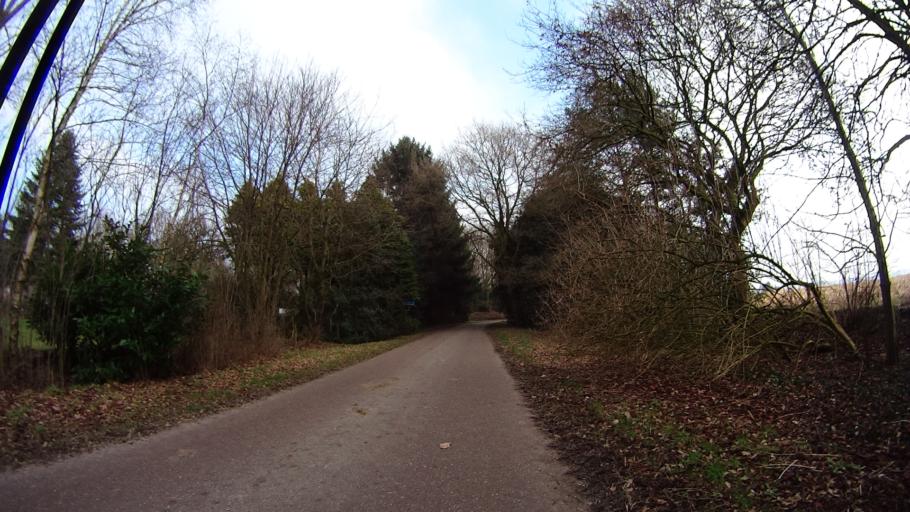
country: NL
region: Drenthe
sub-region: Gemeente Coevorden
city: Sleen
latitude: 52.7561
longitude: 6.8254
